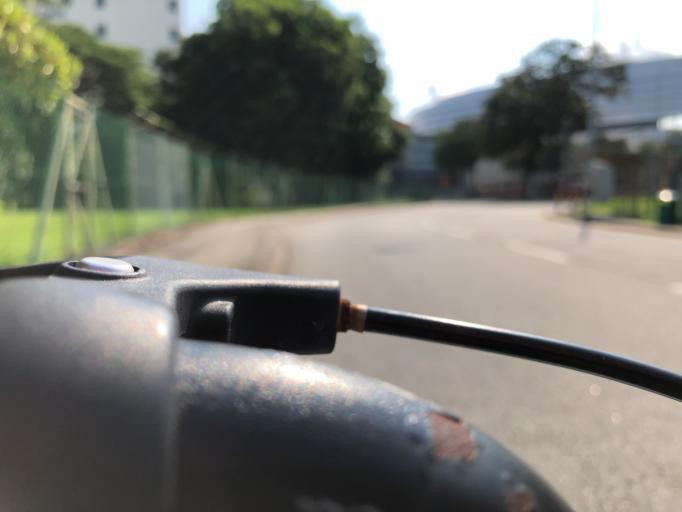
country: SG
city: Singapore
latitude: 1.2937
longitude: 103.7891
